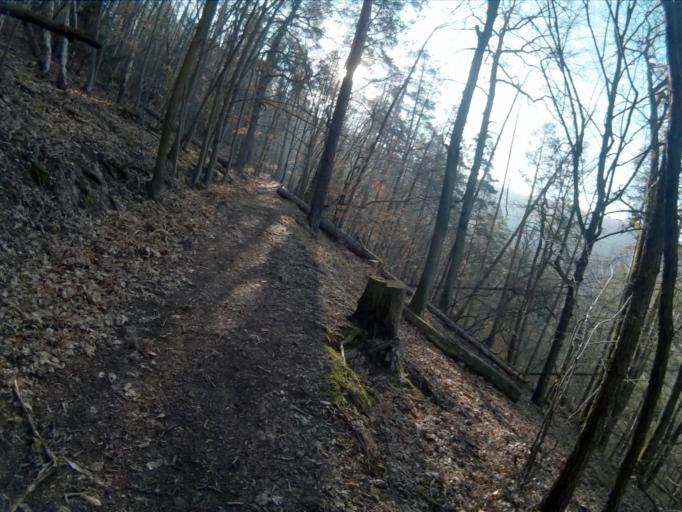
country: CZ
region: Vysocina
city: Namest' nad Oslavou
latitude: 49.1674
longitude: 16.1741
